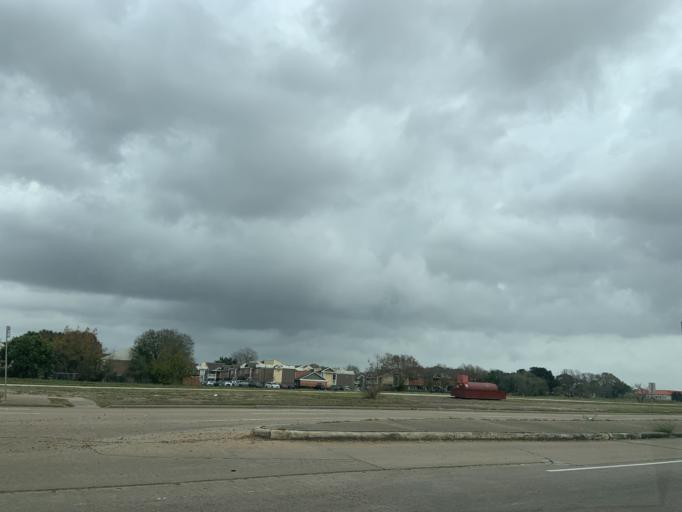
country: US
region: Texas
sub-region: Harris County
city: Bellaire
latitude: 29.6755
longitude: -95.5069
